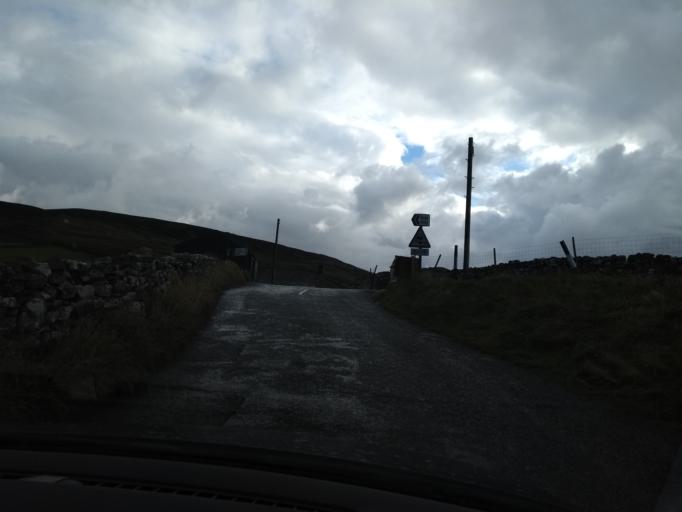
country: GB
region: England
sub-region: County Durham
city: Bowes
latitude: 54.4036
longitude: -2.1668
